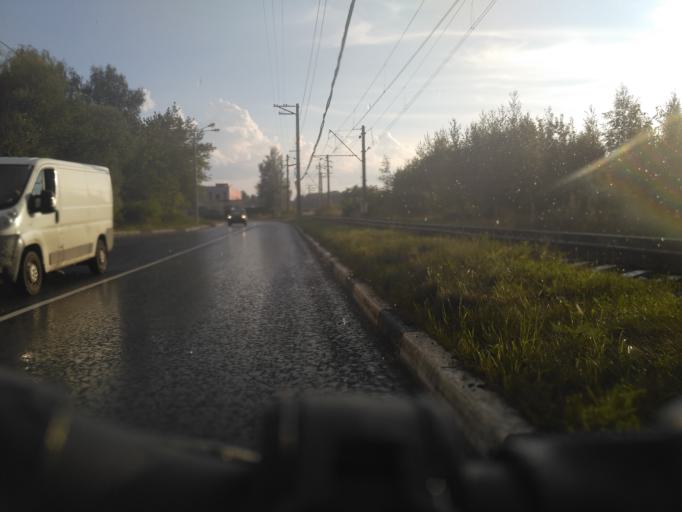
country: RU
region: Moskovskaya
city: Dubna
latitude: 56.7342
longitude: 37.1452
